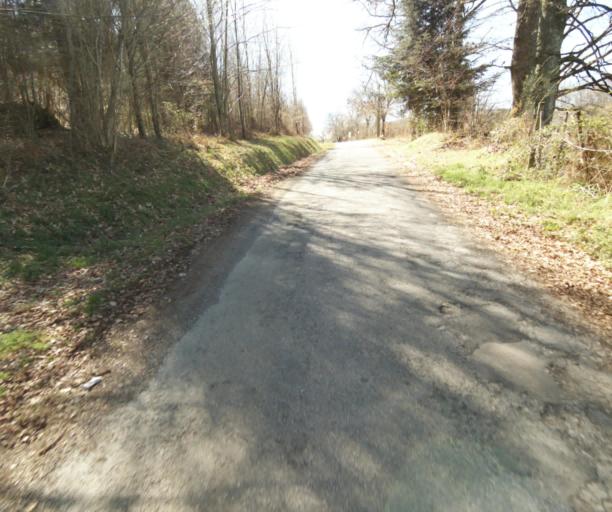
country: FR
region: Limousin
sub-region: Departement de la Correze
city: Seilhac
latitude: 45.3609
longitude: 1.7198
